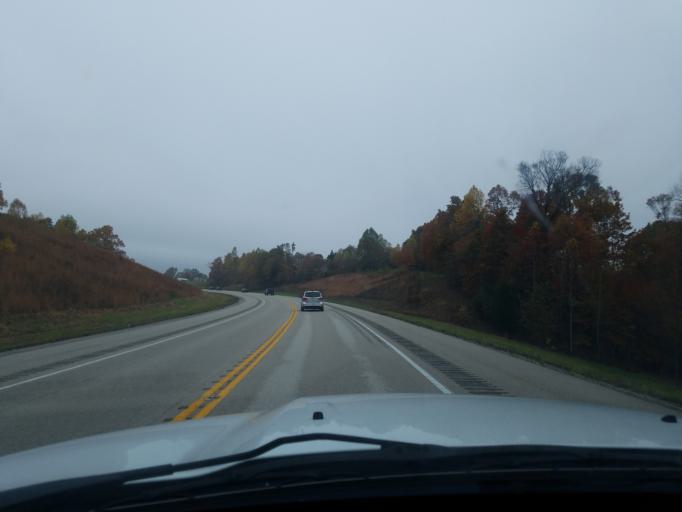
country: US
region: Kentucky
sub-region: Green County
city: Greensburg
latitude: 37.4510
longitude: -85.5295
